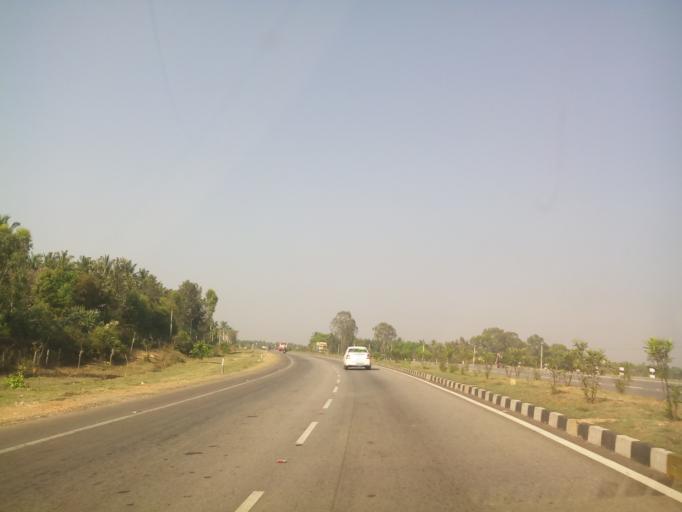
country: IN
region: Karnataka
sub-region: Bangalore Rural
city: Nelamangala
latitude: 13.0657
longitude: 77.3083
